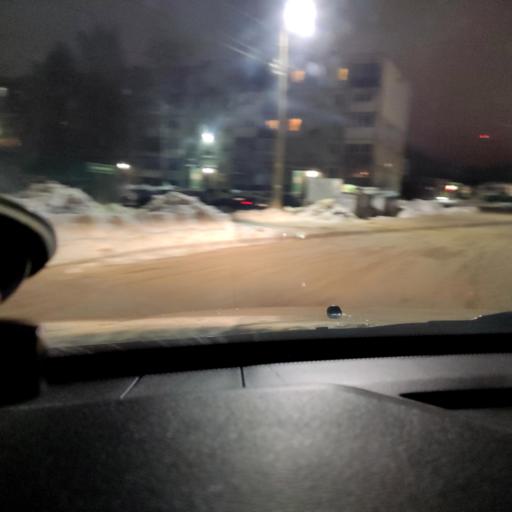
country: RU
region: Samara
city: Smyshlyayevka
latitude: 53.2549
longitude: 50.4849
